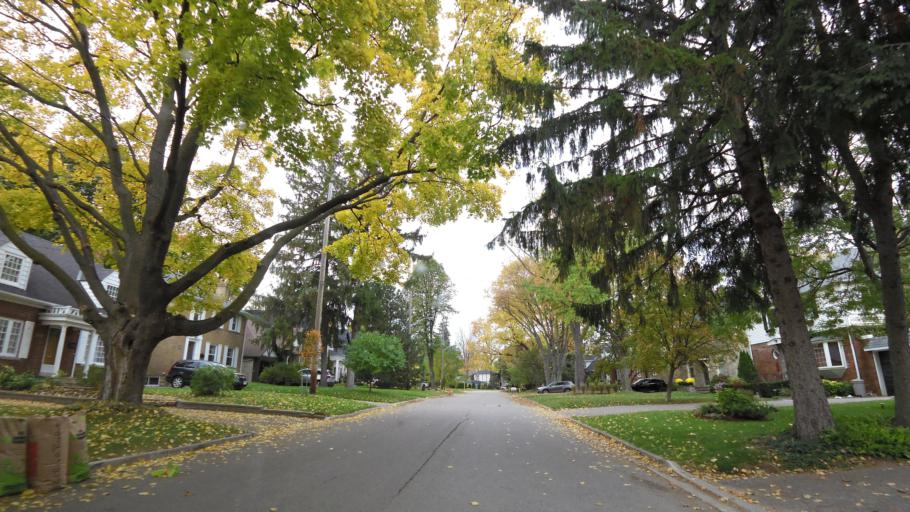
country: CA
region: Ontario
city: Etobicoke
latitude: 43.6487
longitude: -79.5357
